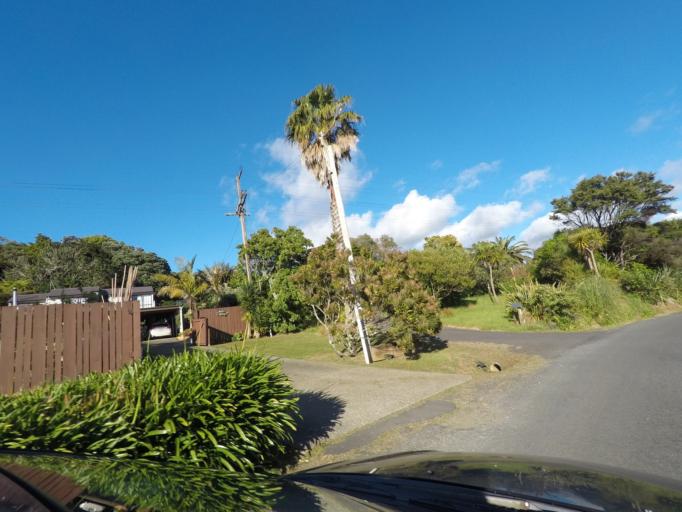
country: NZ
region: Auckland
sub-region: Auckland
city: Titirangi
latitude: -37.0081
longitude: 174.6018
